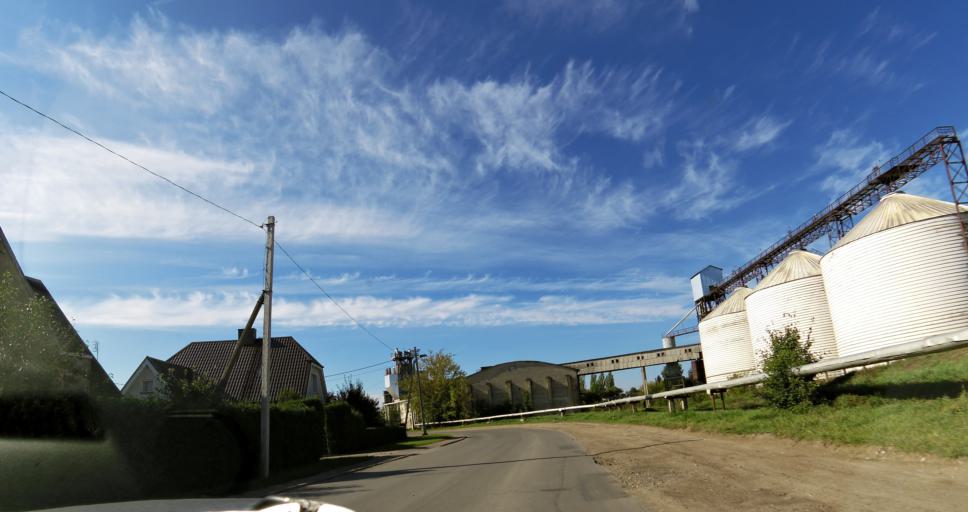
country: LT
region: Panevezys
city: Pasvalys
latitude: 56.0664
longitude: 24.3982
